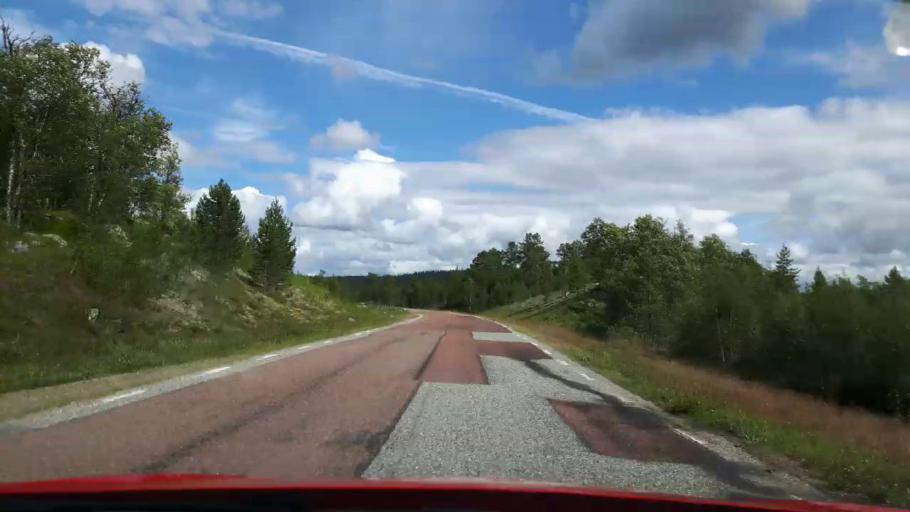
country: NO
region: Hedmark
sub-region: Trysil
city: Innbygda
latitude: 62.1000
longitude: 12.9794
